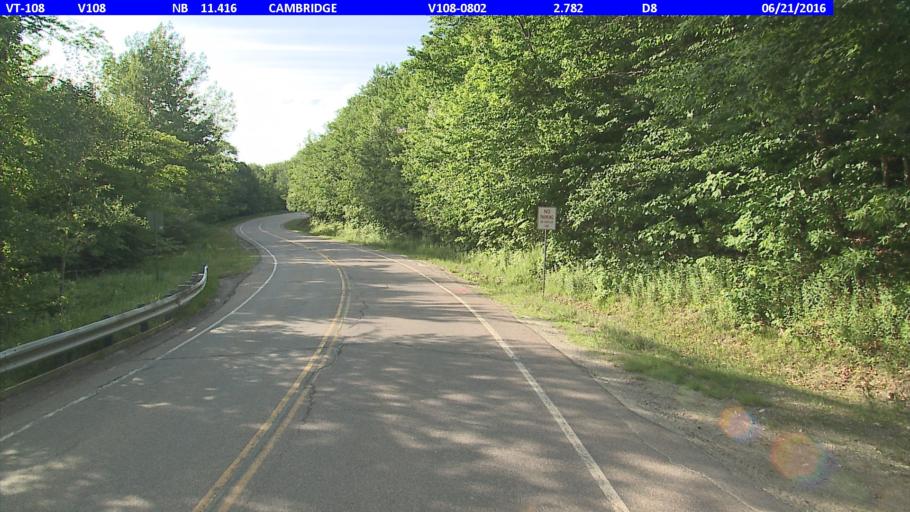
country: US
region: Vermont
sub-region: Lamoille County
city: Johnson
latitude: 44.5738
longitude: -72.7763
